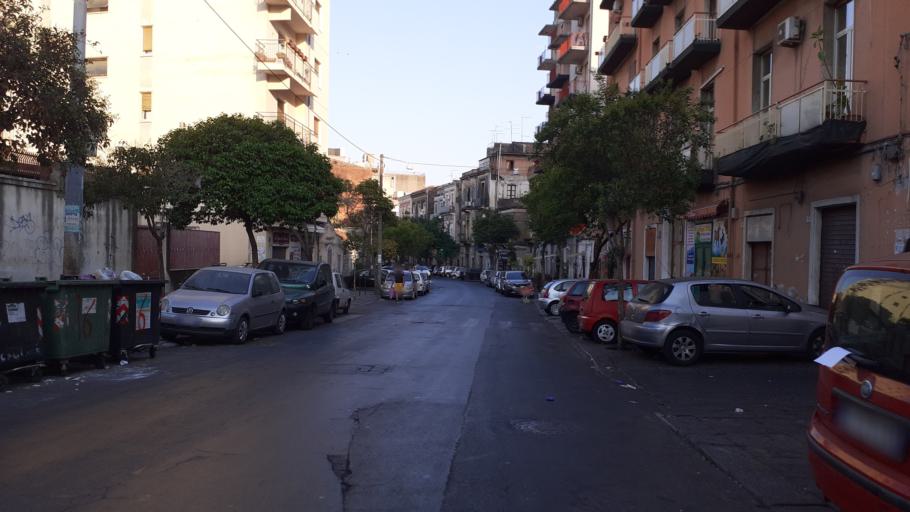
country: IT
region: Sicily
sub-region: Catania
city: Catania
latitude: 37.4994
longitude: 15.0770
